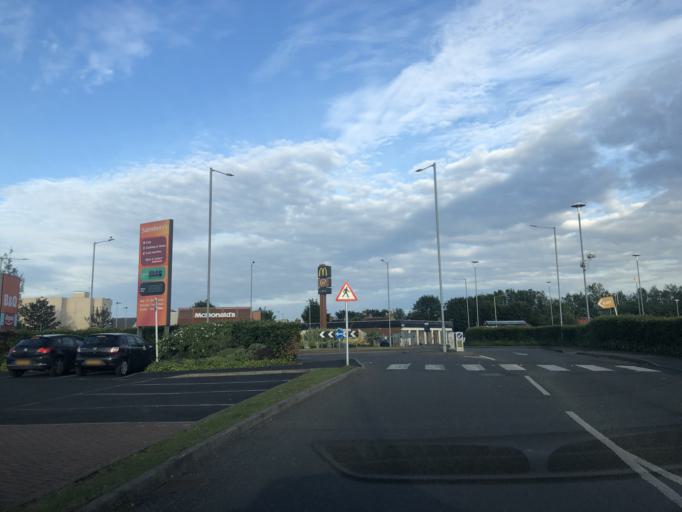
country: GB
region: Scotland
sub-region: Fife
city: Leven
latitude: 56.1943
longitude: -3.0034
